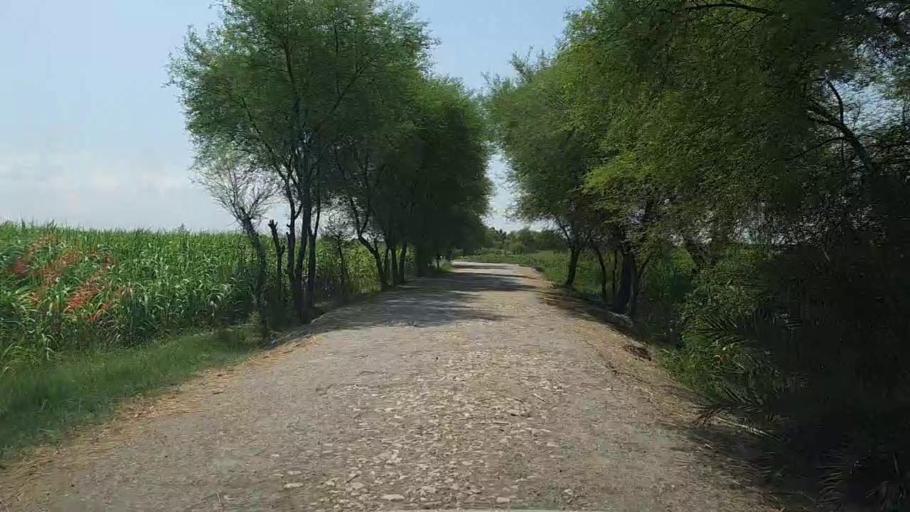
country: PK
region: Sindh
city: Ubauro
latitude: 28.2009
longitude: 69.8026
